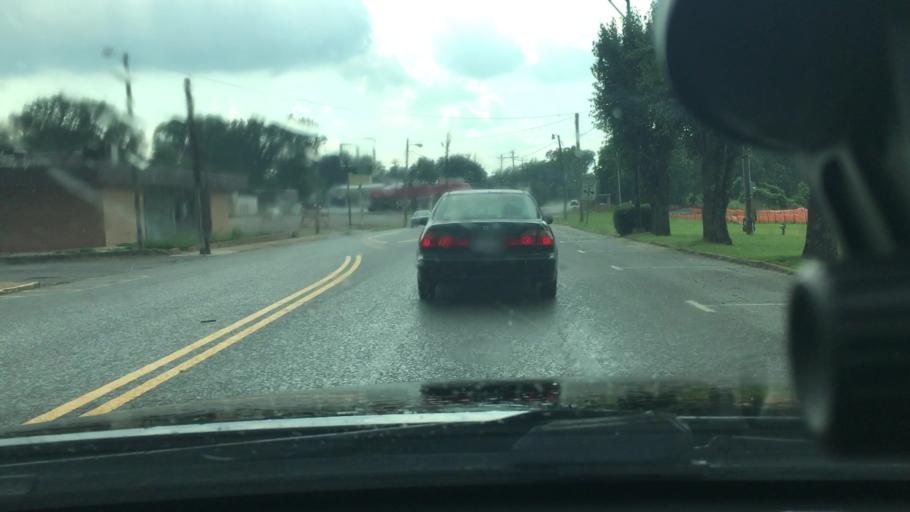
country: US
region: North Carolina
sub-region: Rutherford County
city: Spindale
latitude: 35.3584
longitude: -81.9334
